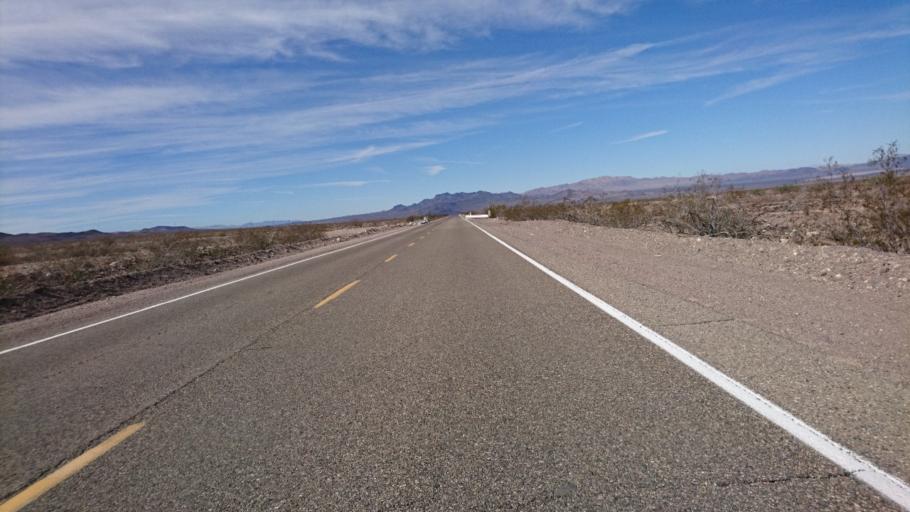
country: US
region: California
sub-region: San Bernardino County
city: Twentynine Palms
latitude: 34.7107
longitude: -116.0912
